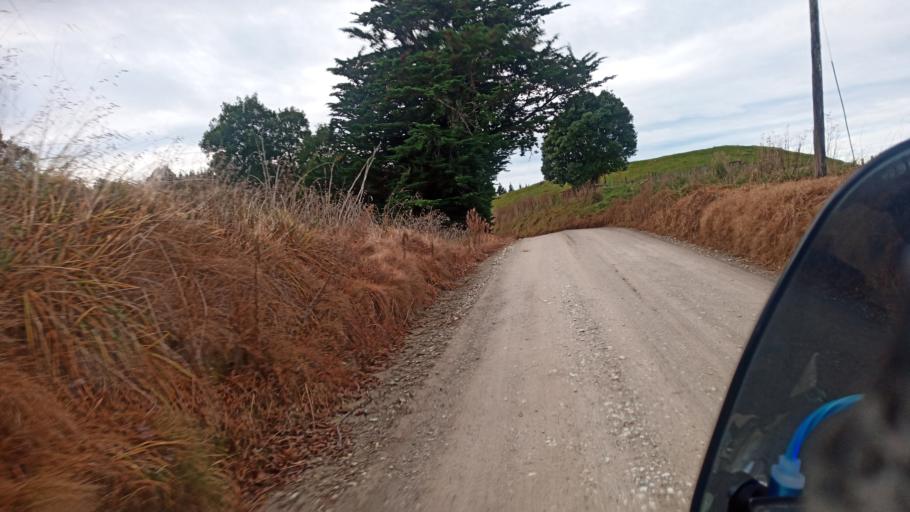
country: NZ
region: Gisborne
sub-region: Gisborne District
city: Gisborne
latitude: -38.3757
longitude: 177.9673
